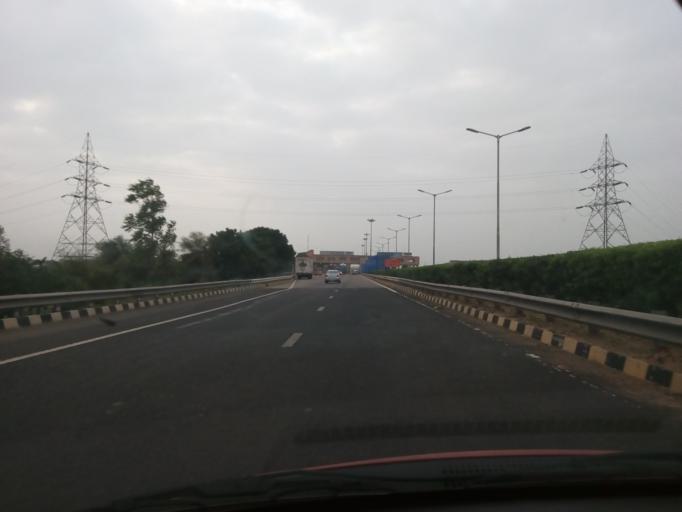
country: IN
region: Gujarat
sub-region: Ahmadabad
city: Ahmedabad
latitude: 22.9774
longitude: 72.6477
